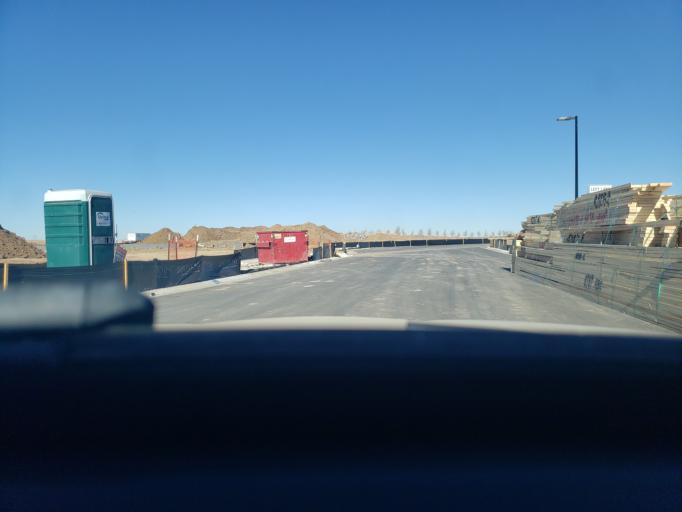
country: US
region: Colorado
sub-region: Adams County
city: Aurora
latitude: 39.7743
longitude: -104.7054
